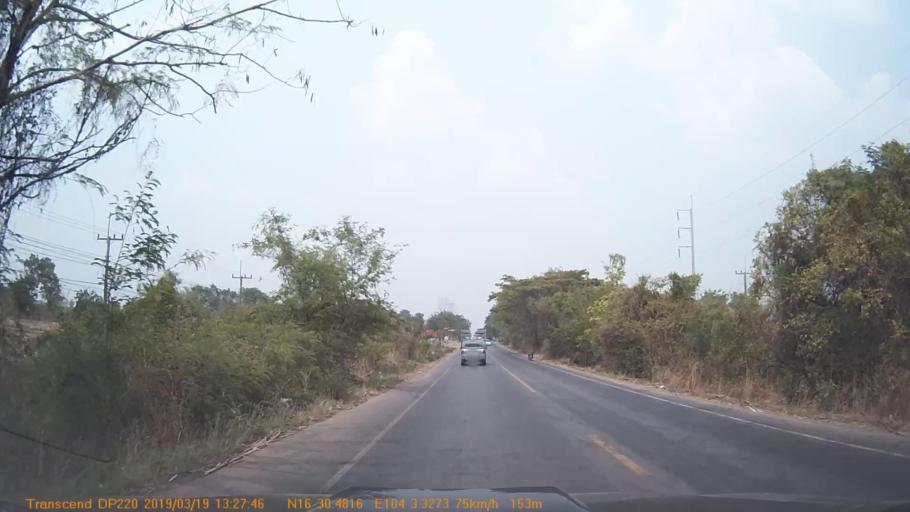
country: TH
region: Kalasin
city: Kuchinarai
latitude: 16.5083
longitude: 104.0555
